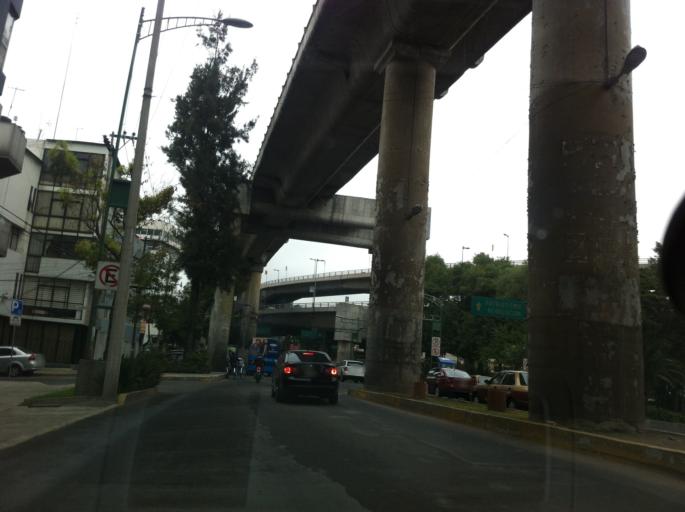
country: MX
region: Mexico City
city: Colonia del Valle
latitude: 19.3852
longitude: -99.1815
